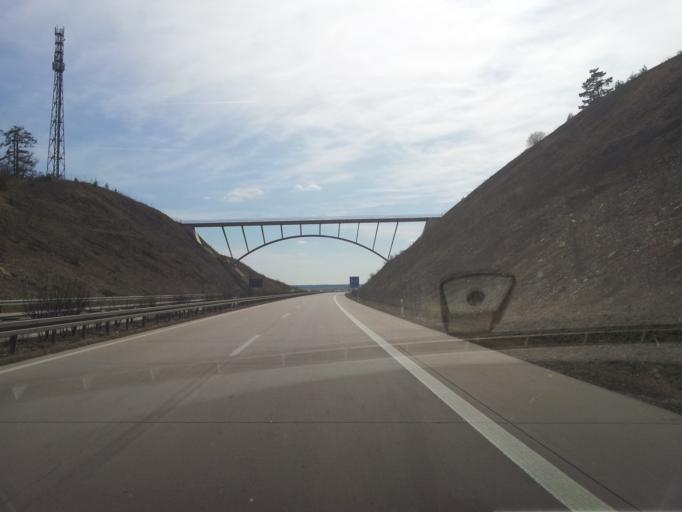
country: DE
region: Thuringia
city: Wolfershausen
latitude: 50.4567
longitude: 10.4511
